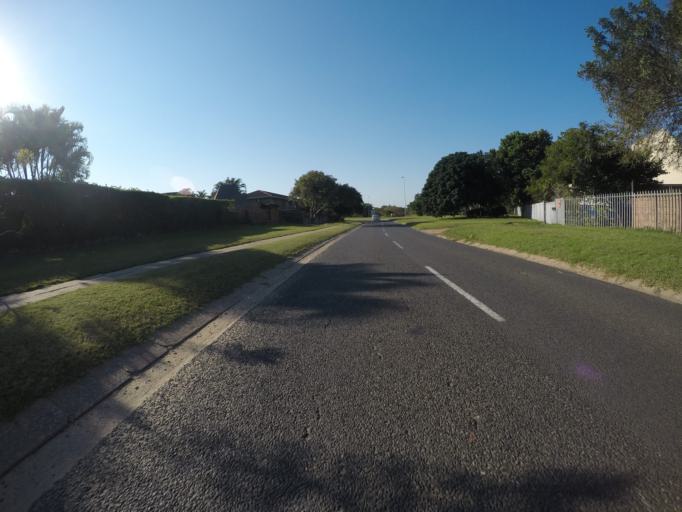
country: ZA
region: KwaZulu-Natal
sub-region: uThungulu District Municipality
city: Richards Bay
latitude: -28.7924
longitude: 32.0976
